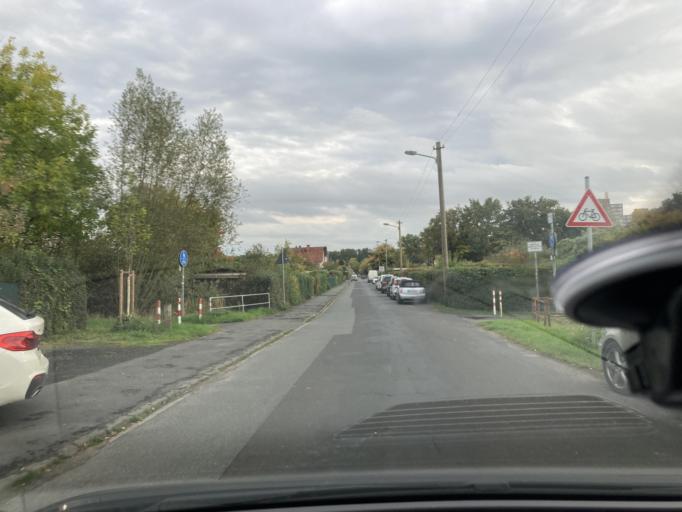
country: DE
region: Hesse
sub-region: Regierungsbezirk Darmstadt
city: Offenbach
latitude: 50.0879
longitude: 8.7780
